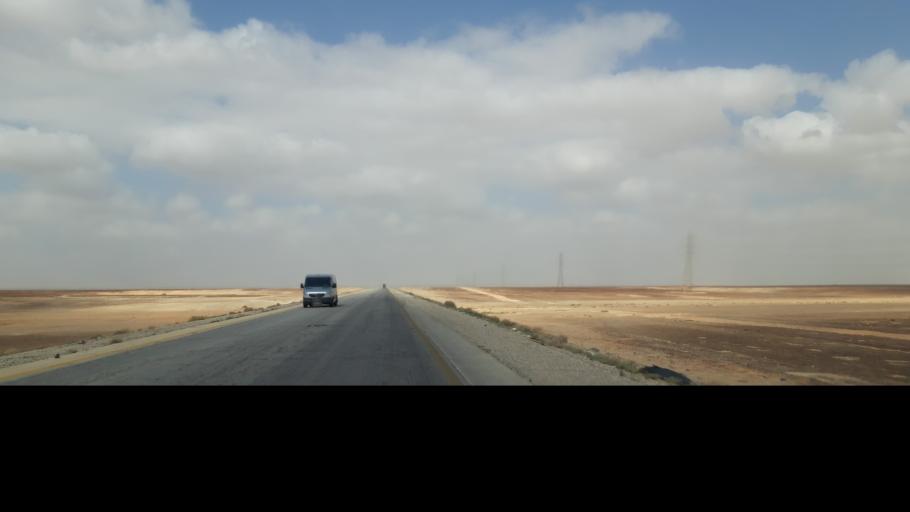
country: JO
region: Amman
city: Al Azraq ash Shamali
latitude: 31.7791
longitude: 36.5720
